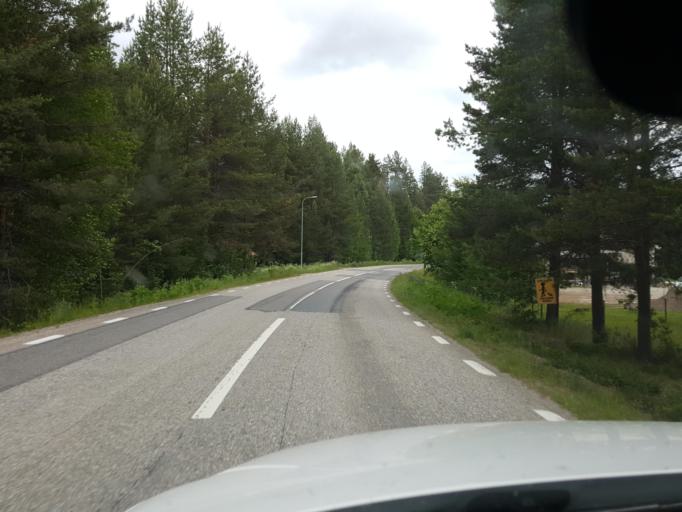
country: SE
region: Gaevleborg
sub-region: Ljusdals Kommun
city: Farila
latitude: 61.7927
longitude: 15.6446
